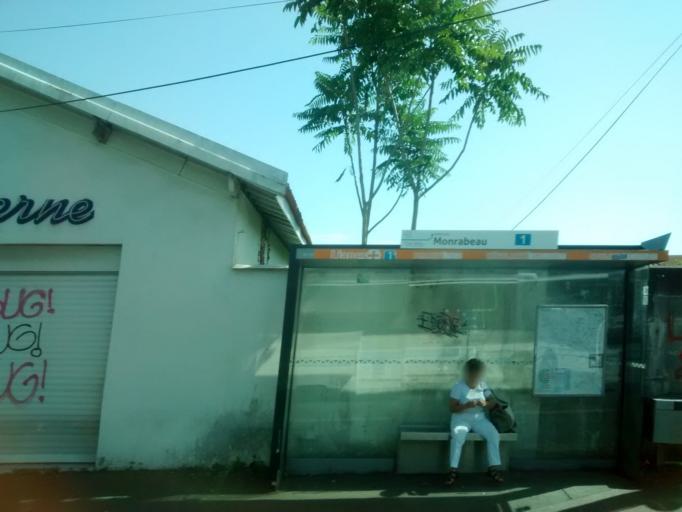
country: FR
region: Aquitaine
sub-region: Departement de la Gironde
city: Merignac
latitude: 44.8387
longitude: -0.6241
